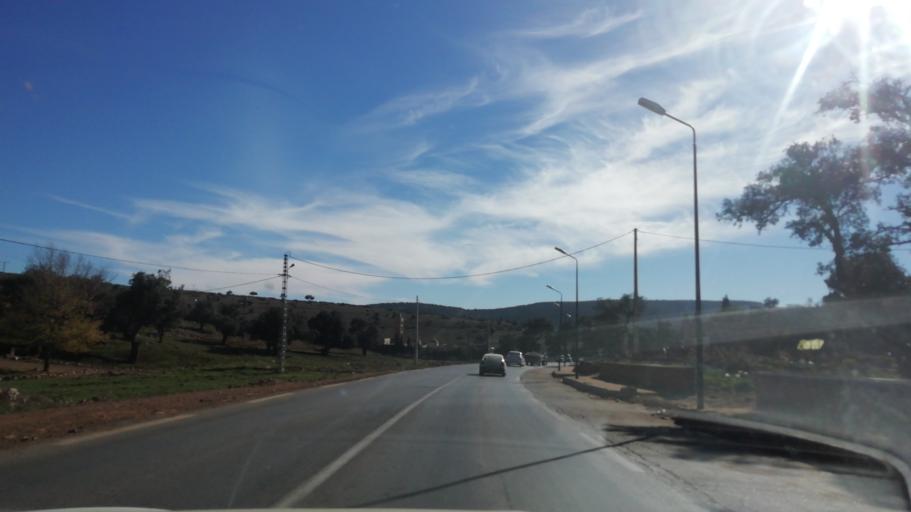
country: DZ
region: Tlemcen
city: Sebdou
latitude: 34.7281
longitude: -1.3372
